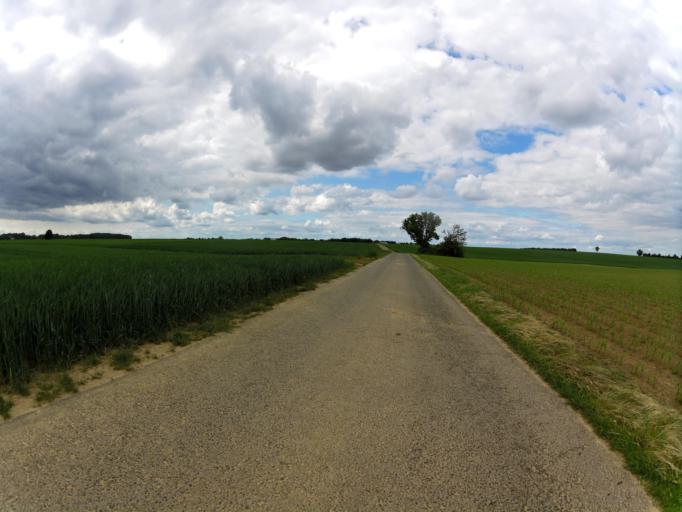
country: DE
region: Bavaria
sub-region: Regierungsbezirk Unterfranken
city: Gaukonigshofen
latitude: 49.6539
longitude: 10.0039
